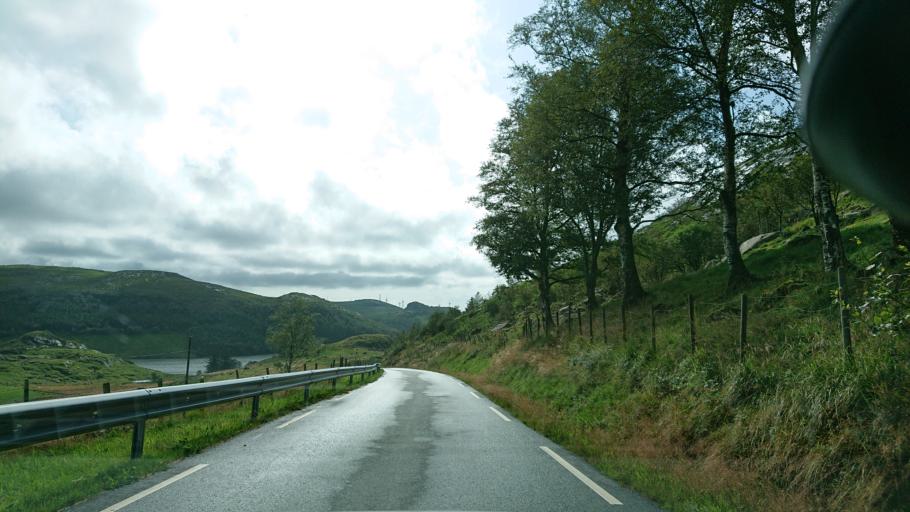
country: NO
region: Rogaland
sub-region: Gjesdal
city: Algard
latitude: 58.6793
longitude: 5.8494
